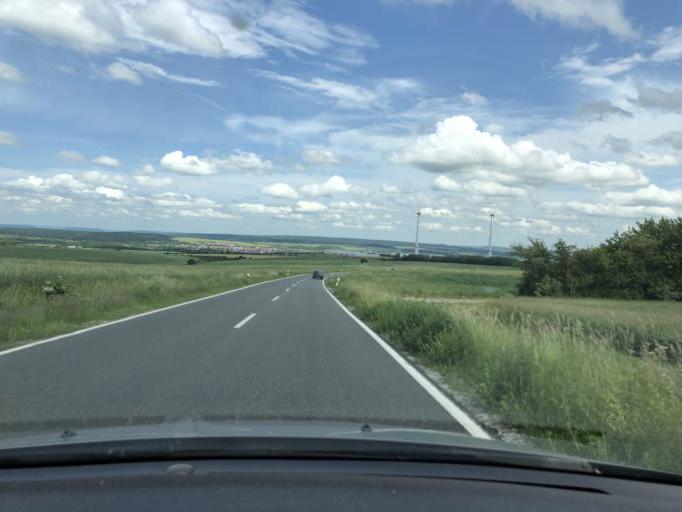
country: DE
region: Thuringia
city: Wachstedt
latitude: 51.2956
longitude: 10.2587
